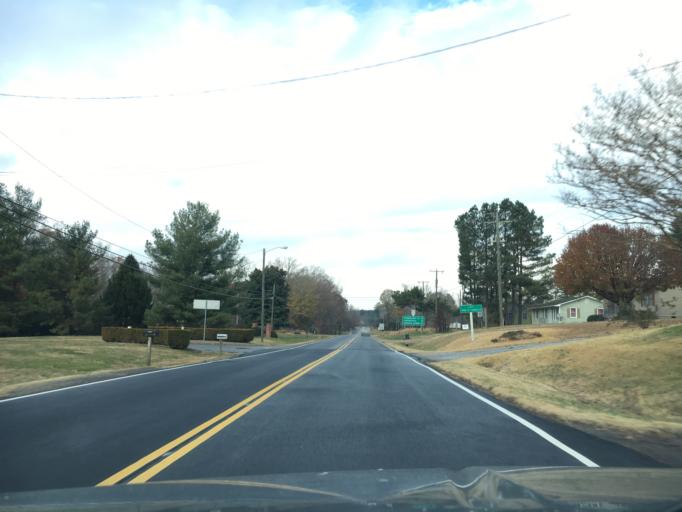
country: US
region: Virginia
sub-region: Prince Edward County
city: Farmville
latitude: 37.3195
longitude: -78.3857
